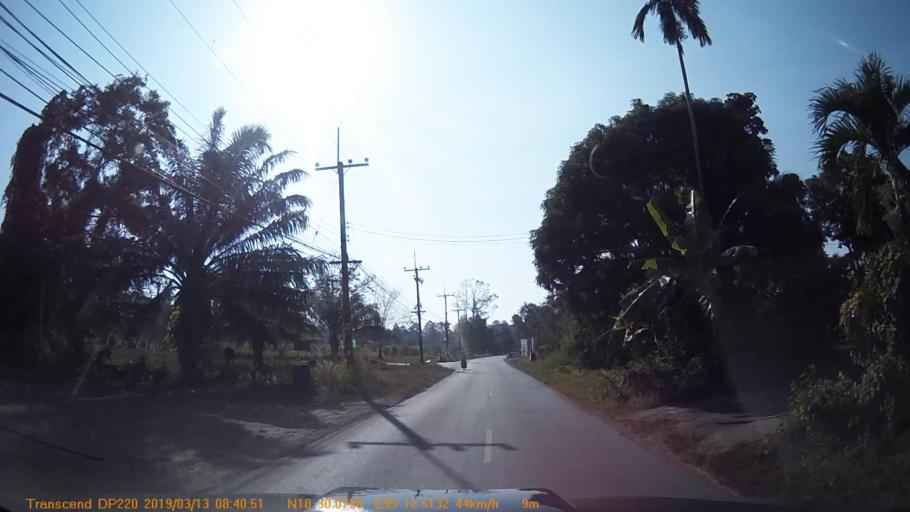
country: TH
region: Chumphon
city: Chumphon
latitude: 10.5012
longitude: 99.2087
